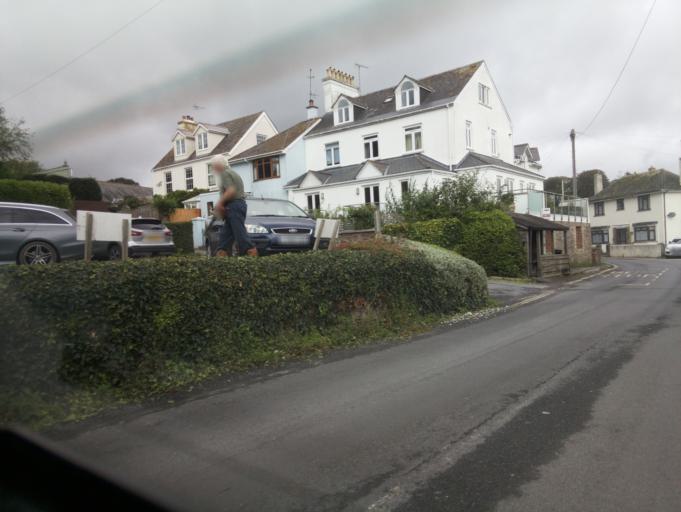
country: GB
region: England
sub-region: Devon
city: Dartmouth
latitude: 50.3236
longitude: -3.5985
